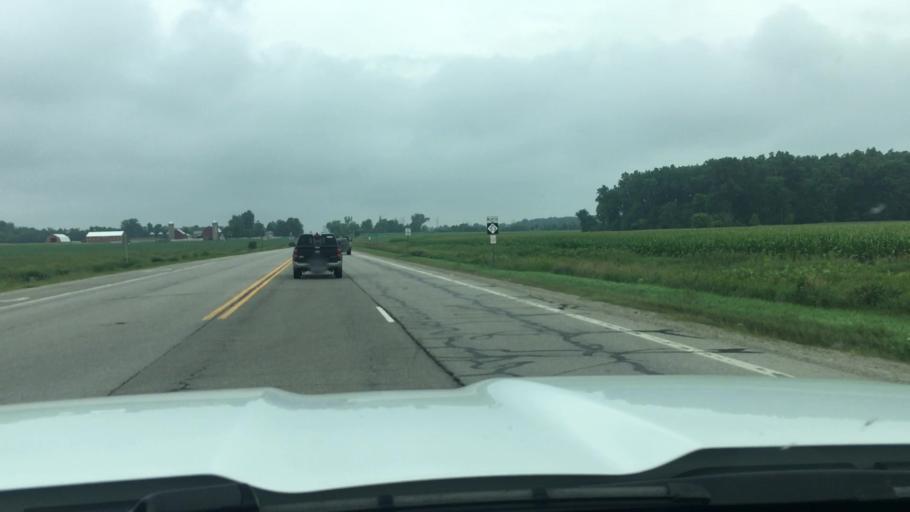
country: US
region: Michigan
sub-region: Sanilac County
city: Brown City
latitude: 43.2322
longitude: -83.0781
